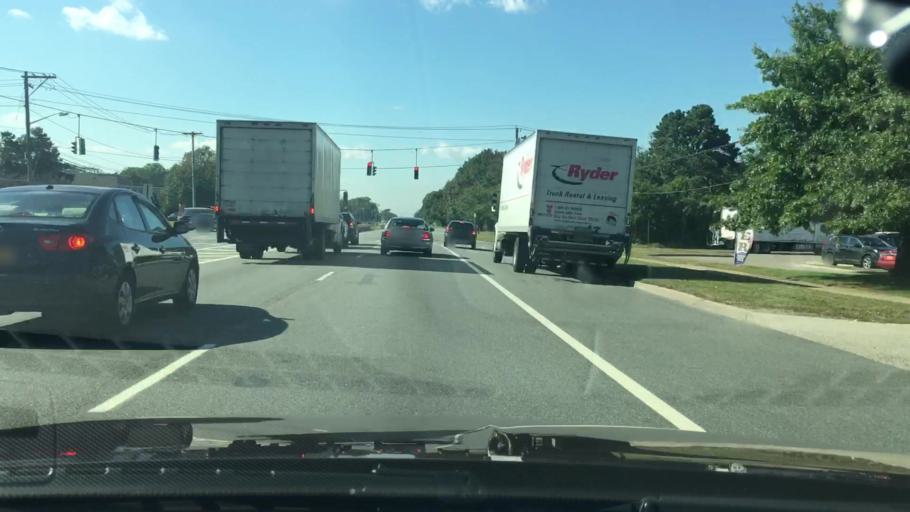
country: US
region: New York
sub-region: Suffolk County
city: Bohemia
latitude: 40.7875
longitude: -73.1295
